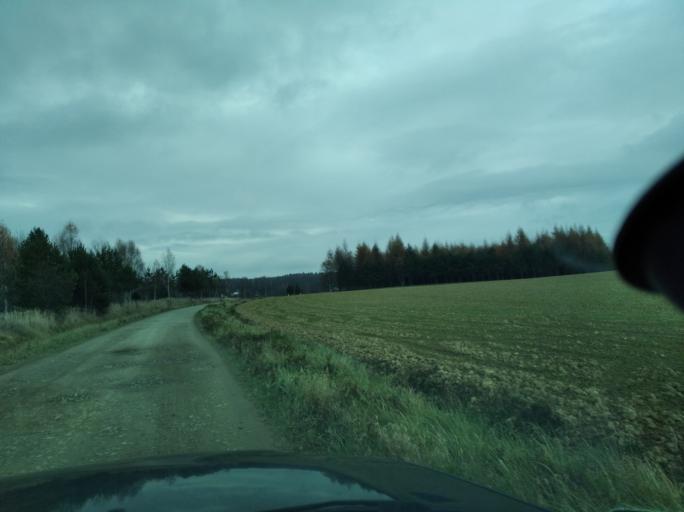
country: PL
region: Subcarpathian Voivodeship
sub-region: Powiat strzyzowski
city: Wysoka Strzyzowska
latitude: 49.8031
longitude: 21.7814
